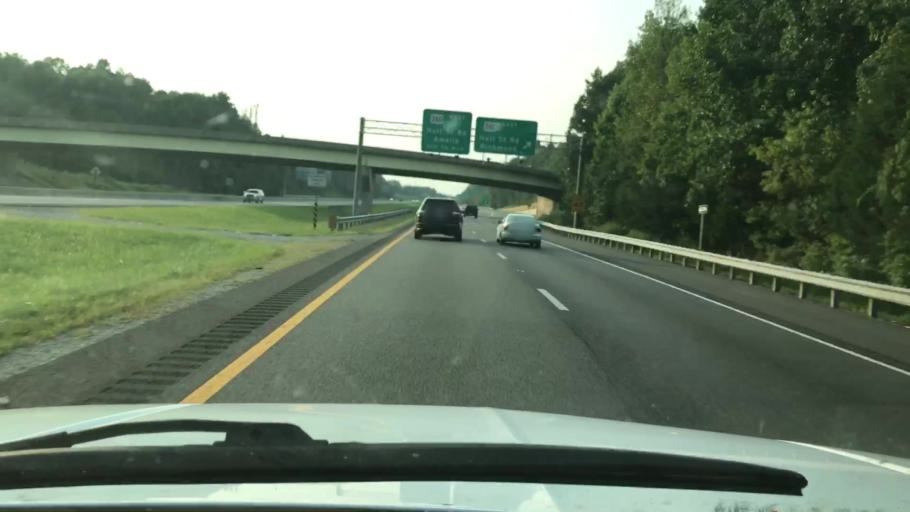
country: US
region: Virginia
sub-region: Chesterfield County
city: Brandermill
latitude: 37.4155
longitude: -77.6214
